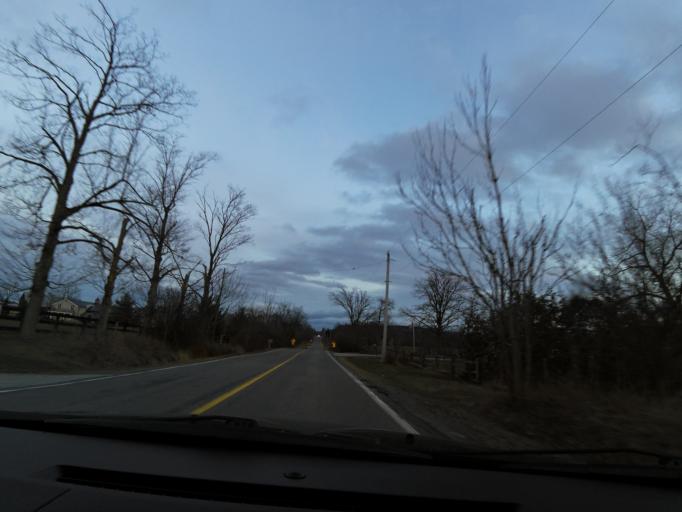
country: CA
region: Ontario
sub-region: Halton
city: Milton
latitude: 43.4488
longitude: -79.9037
